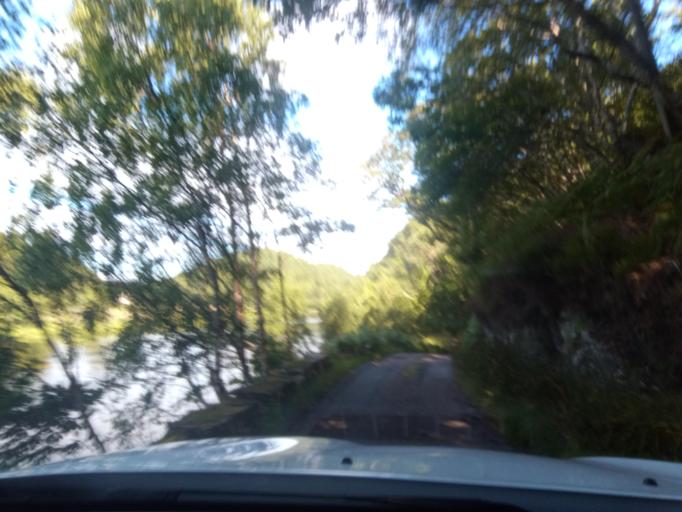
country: GB
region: Scotland
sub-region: Argyll and Bute
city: Isle Of Mull
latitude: 56.7623
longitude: -5.8190
